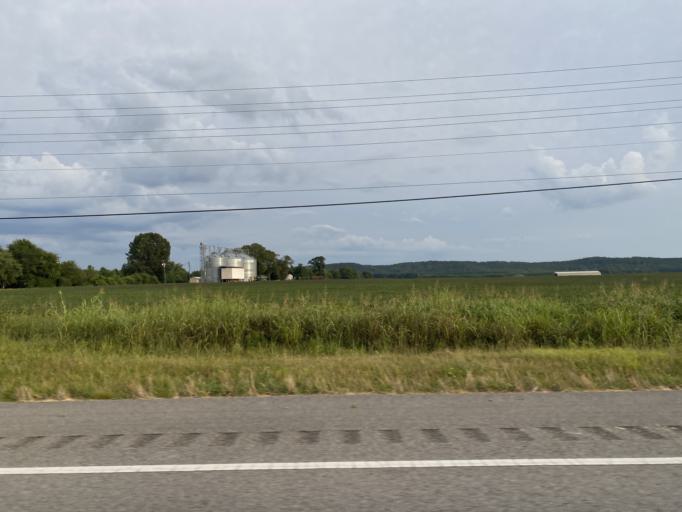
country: US
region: Alabama
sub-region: Franklin County
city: Red Bay
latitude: 34.4479
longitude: -88.0873
